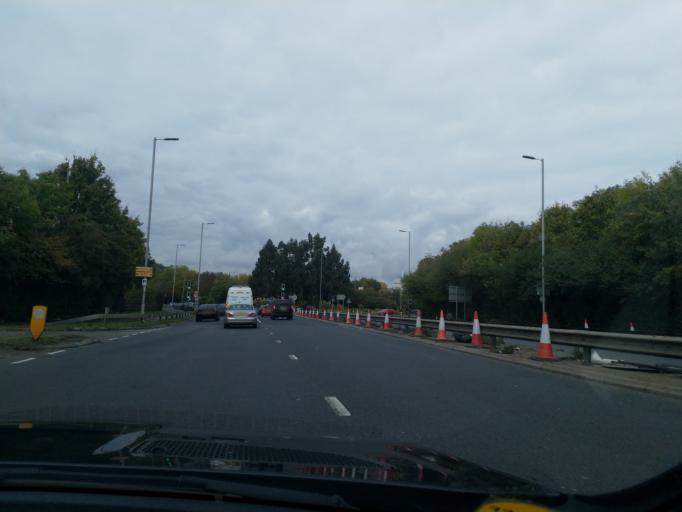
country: GB
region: England
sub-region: Greater London
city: Hayes
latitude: 51.4967
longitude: -0.4096
